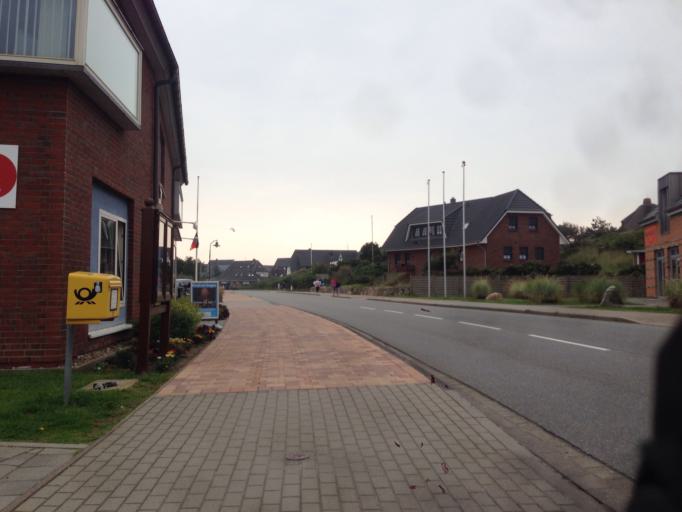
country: DE
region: Schleswig-Holstein
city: Norddorf
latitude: 54.7577
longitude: 8.2861
